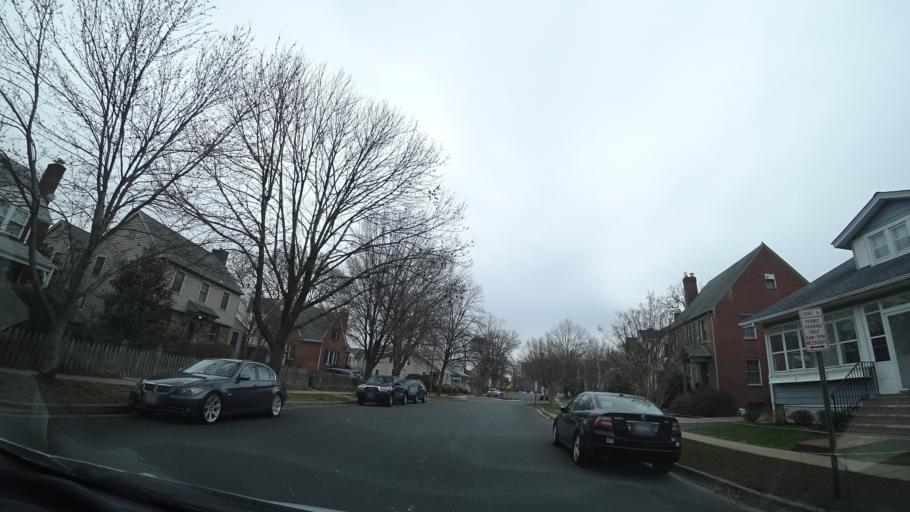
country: US
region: Virginia
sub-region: Arlington County
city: Arlington
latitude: 38.8924
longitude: -77.0917
